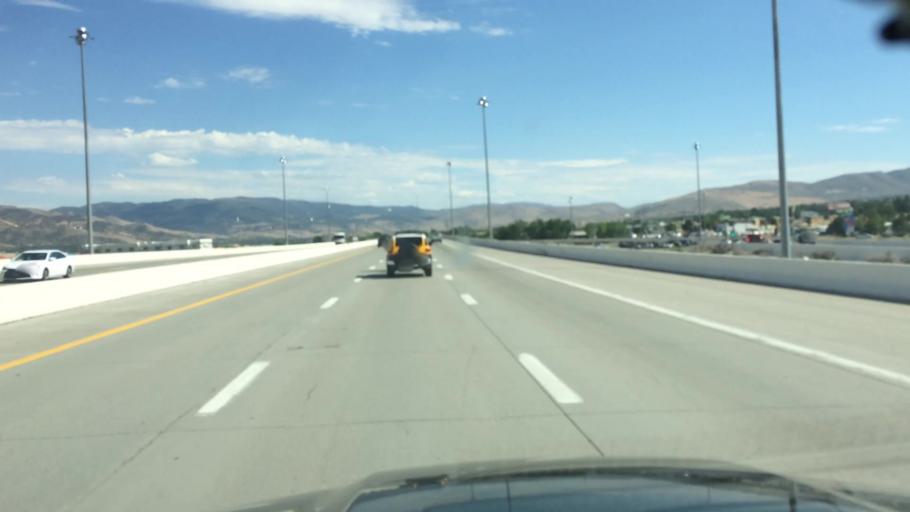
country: US
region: Nevada
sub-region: Washoe County
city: Sparks
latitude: 39.4421
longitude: -119.7668
